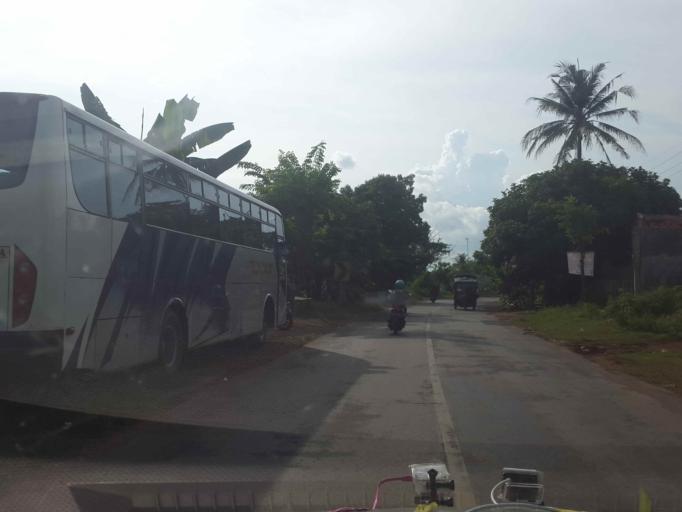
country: ID
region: East Java
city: Kebunkelapa
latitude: -7.0447
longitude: 113.9254
